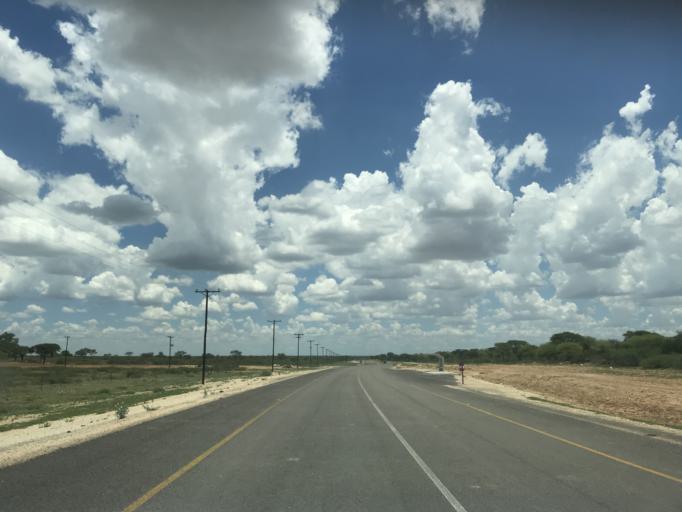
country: BW
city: Mabuli
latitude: -25.7879
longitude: 24.9018
